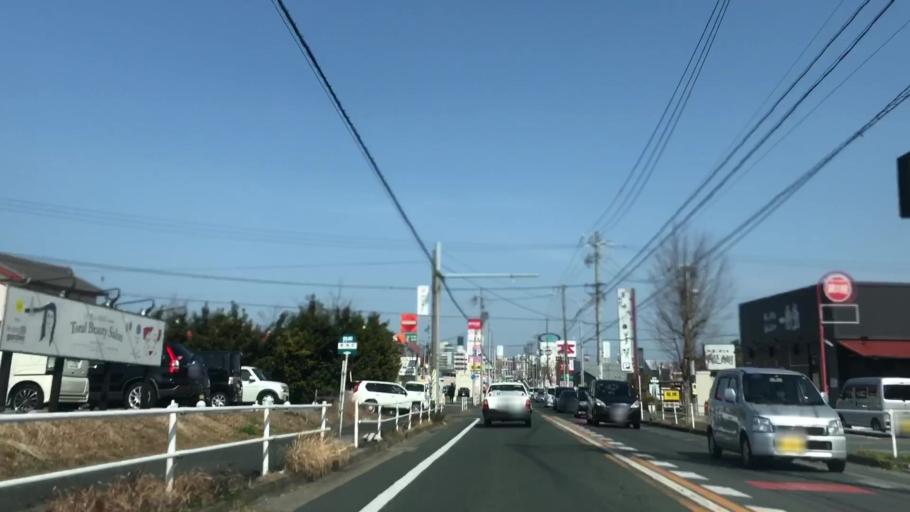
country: JP
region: Aichi
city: Toyohashi
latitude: 34.7500
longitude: 137.3768
